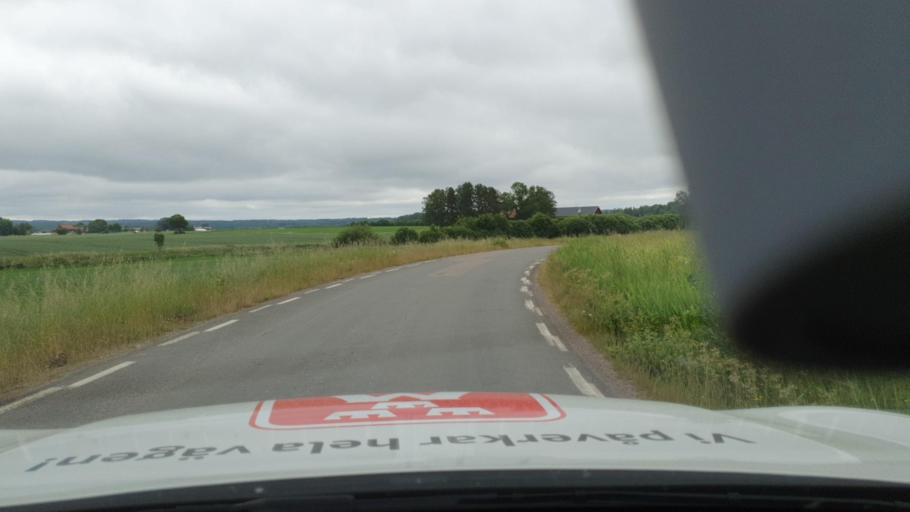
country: SE
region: Vaestra Goetaland
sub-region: Tibro Kommun
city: Tibro
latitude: 58.3883
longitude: 14.1195
